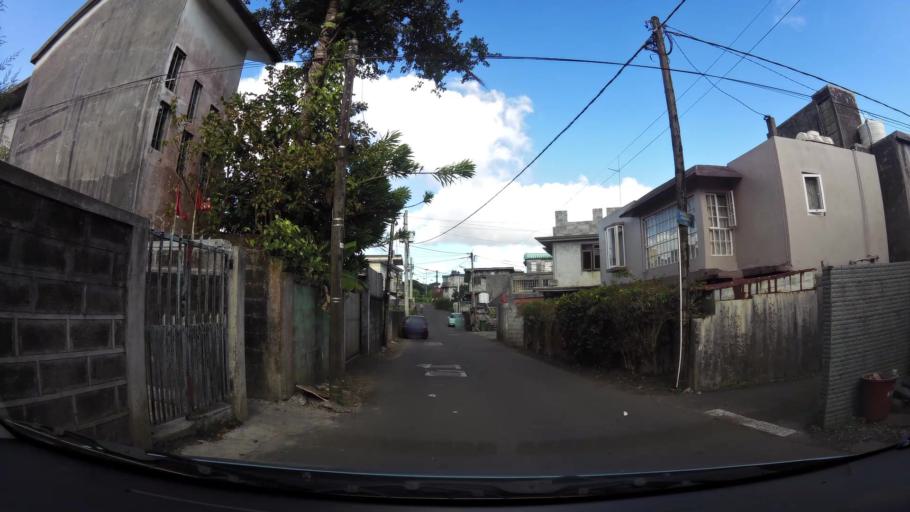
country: MU
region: Plaines Wilhems
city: Curepipe
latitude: -20.3071
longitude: 57.5186
